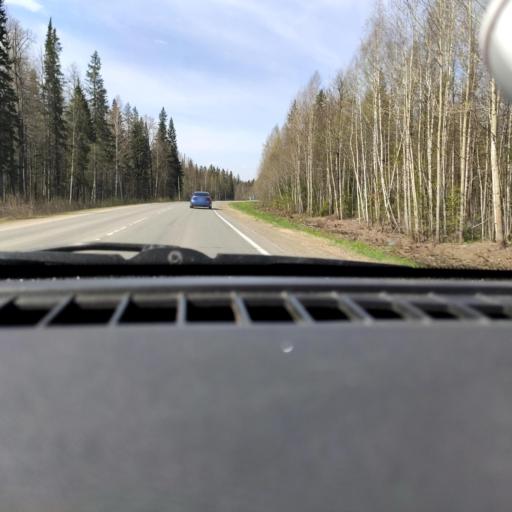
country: RU
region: Perm
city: Perm
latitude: 58.2164
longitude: 56.1730
